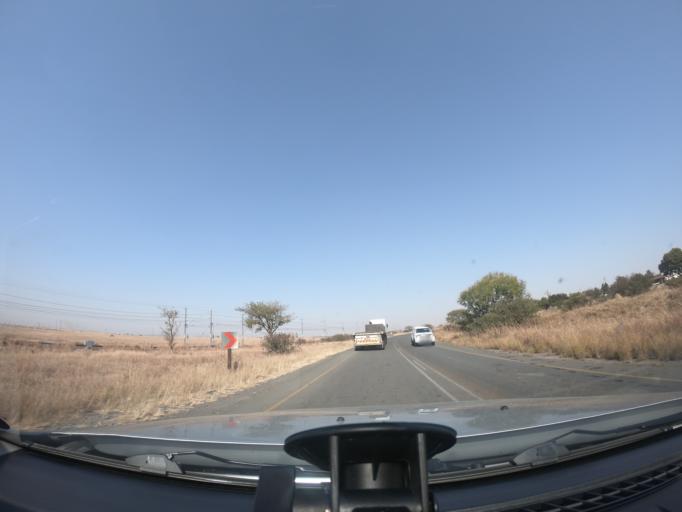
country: ZA
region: KwaZulu-Natal
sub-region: uThukela District Municipality
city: Ladysmith
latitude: -28.7536
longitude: 29.8228
